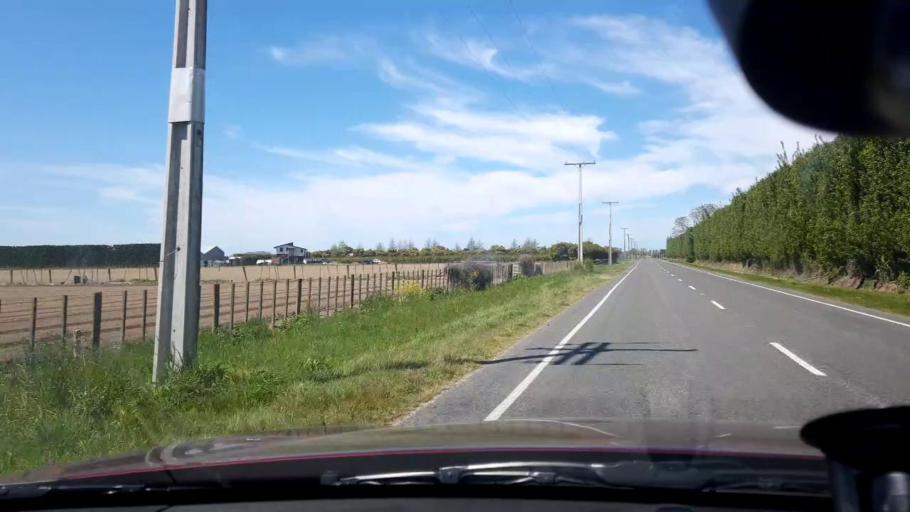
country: NZ
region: Gisborne
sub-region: Gisborne District
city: Gisborne
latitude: -38.6269
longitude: 177.9246
